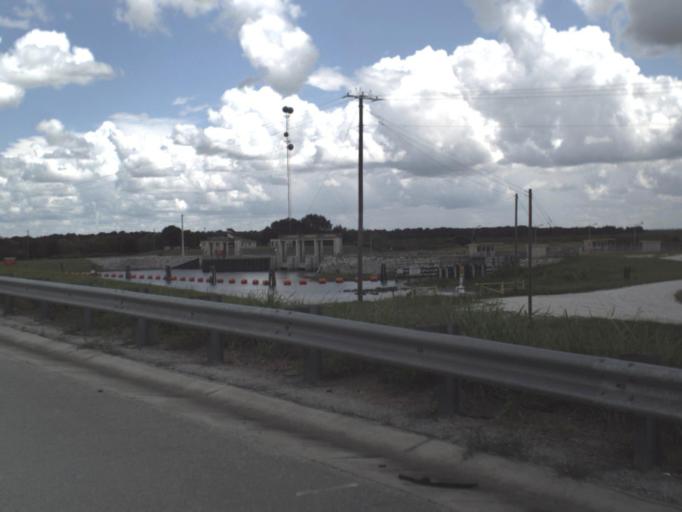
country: US
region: Florida
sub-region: Polk County
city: Babson Park
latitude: 27.8049
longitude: -81.1999
